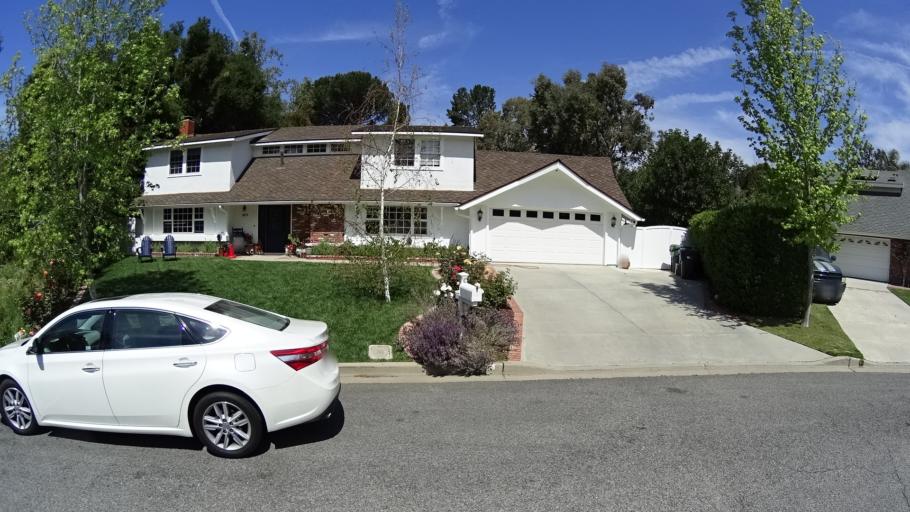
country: US
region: California
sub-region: Ventura County
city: Thousand Oaks
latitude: 34.2029
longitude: -118.8420
